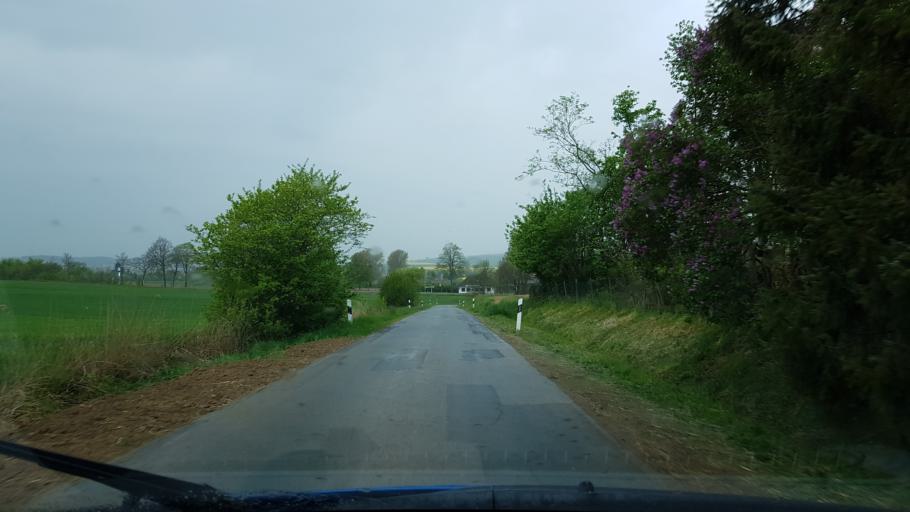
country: DE
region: Lower Saxony
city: Einbeck
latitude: 51.8639
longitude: 9.8772
